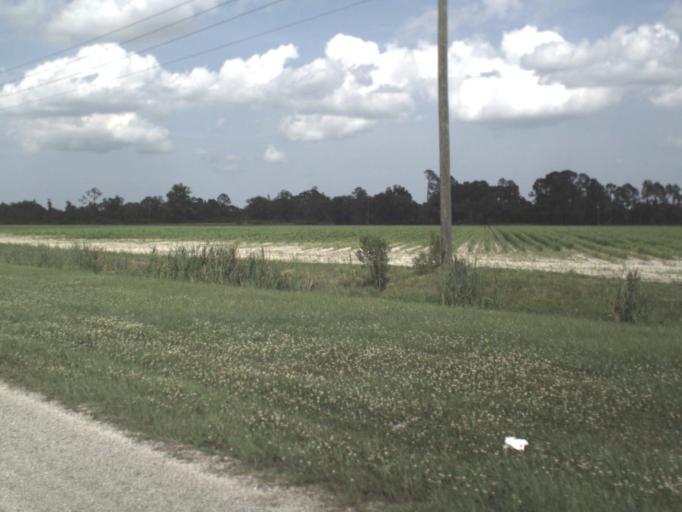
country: US
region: Florida
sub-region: Putnam County
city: East Palatka
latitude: 29.6757
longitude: -81.5830
